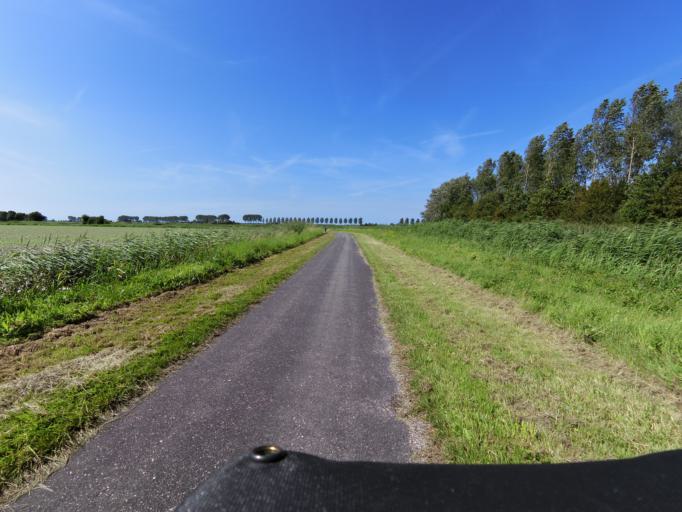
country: NL
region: South Holland
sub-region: Gemeente Goeree-Overflakkee
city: Dirksland
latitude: 51.7137
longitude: 4.1357
